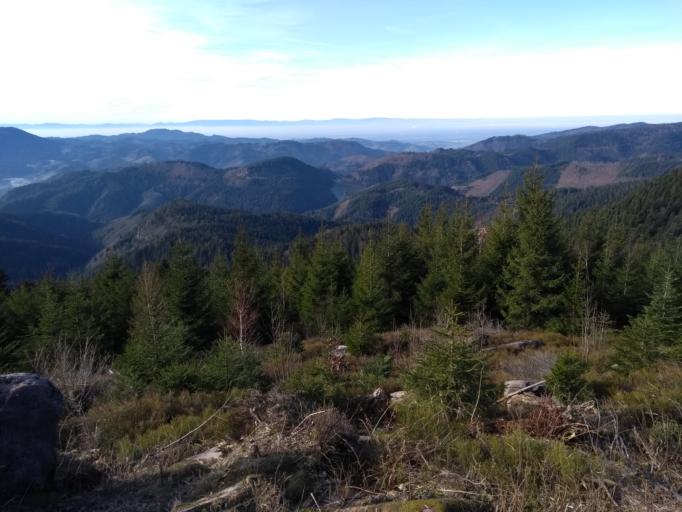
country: DE
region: Baden-Wuerttemberg
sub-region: Freiburg Region
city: Bad Peterstal-Griesbach
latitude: 48.4978
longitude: 8.2261
